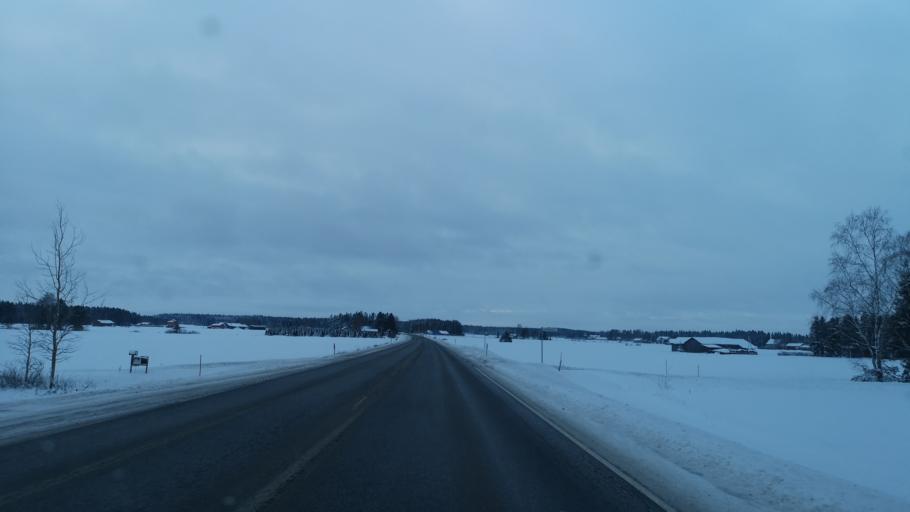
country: FI
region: Varsinais-Suomi
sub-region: Loimaa
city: Loimaa
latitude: 60.8896
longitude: 23.1013
